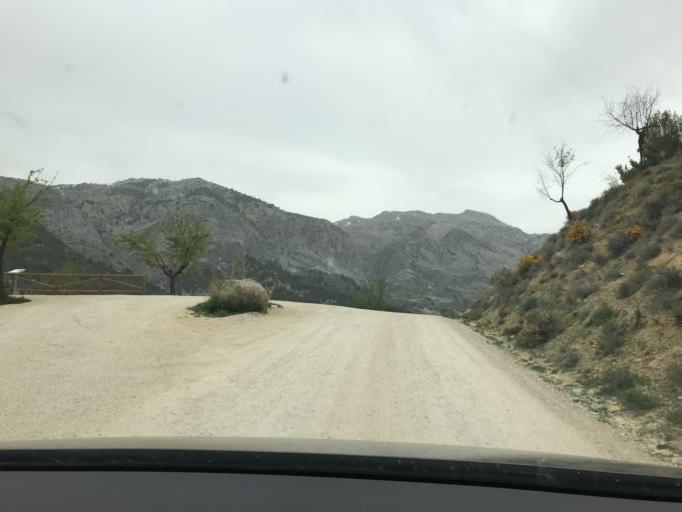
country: ES
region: Andalusia
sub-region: Provincia de Granada
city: Castril
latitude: 37.8264
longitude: -2.7723
